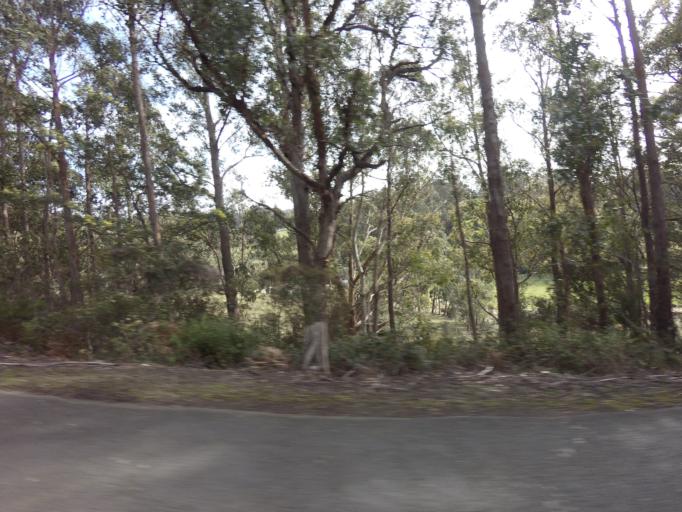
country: AU
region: Tasmania
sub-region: Kingborough
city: Margate
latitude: -43.0026
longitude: 147.1748
